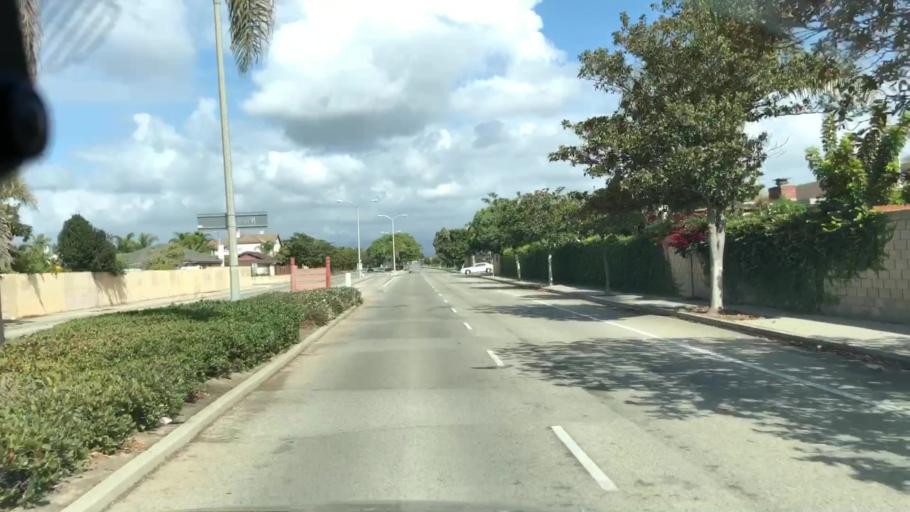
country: US
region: California
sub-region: Ventura County
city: Oxnard
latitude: 34.1925
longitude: -119.2079
